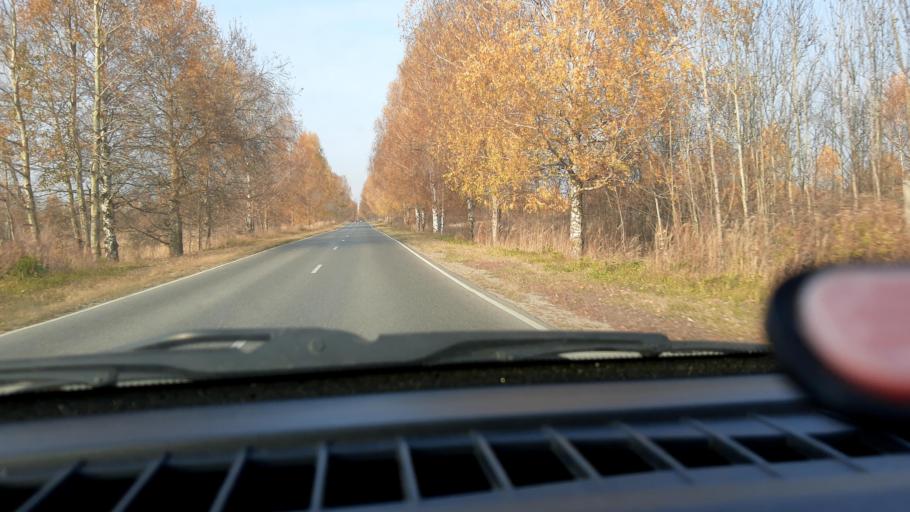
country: RU
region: Nizjnij Novgorod
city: Neklyudovo
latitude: 56.5119
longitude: 43.8398
